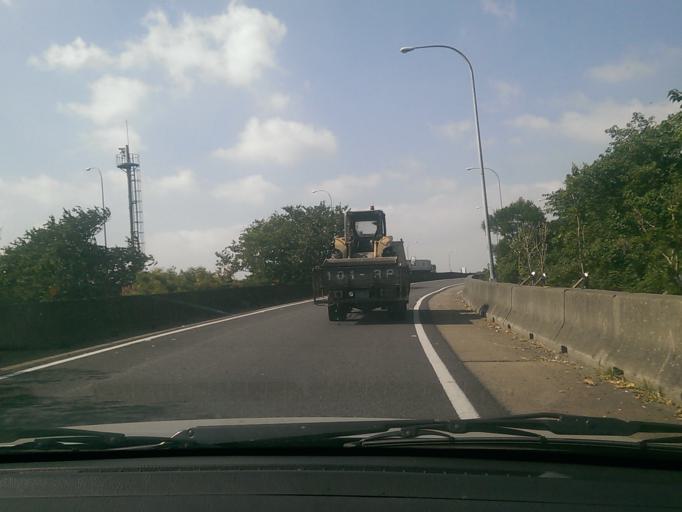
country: TW
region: Taiwan
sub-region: Changhua
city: Chang-hua
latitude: 23.9541
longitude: 120.5074
